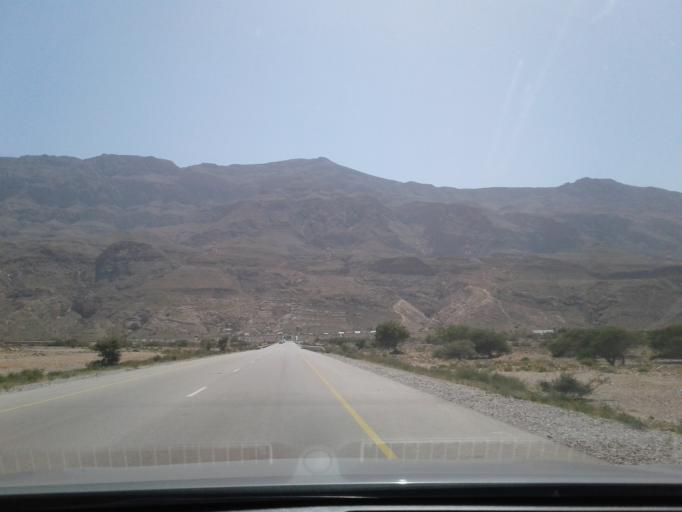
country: OM
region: Ash Sharqiyah
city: Al Qabil
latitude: 23.0301
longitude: 59.0809
